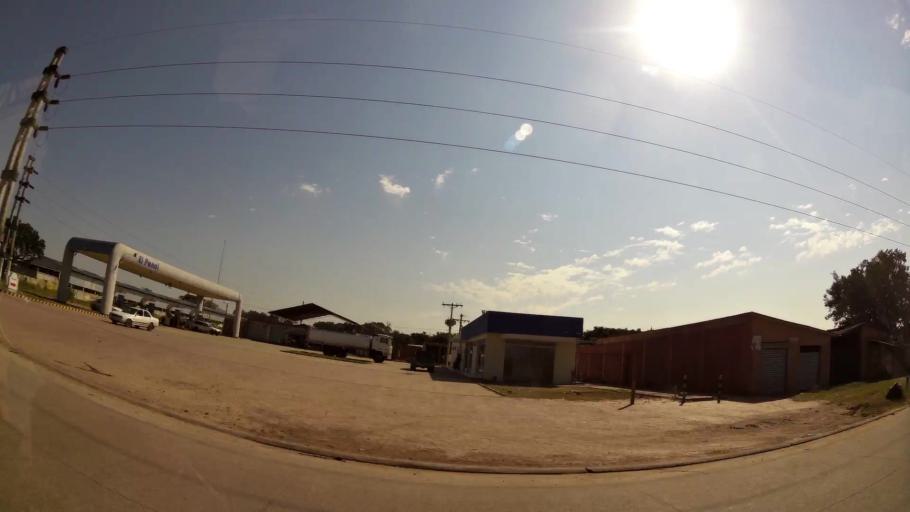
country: BO
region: Santa Cruz
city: Cotoca
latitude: -17.7861
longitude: -63.1082
